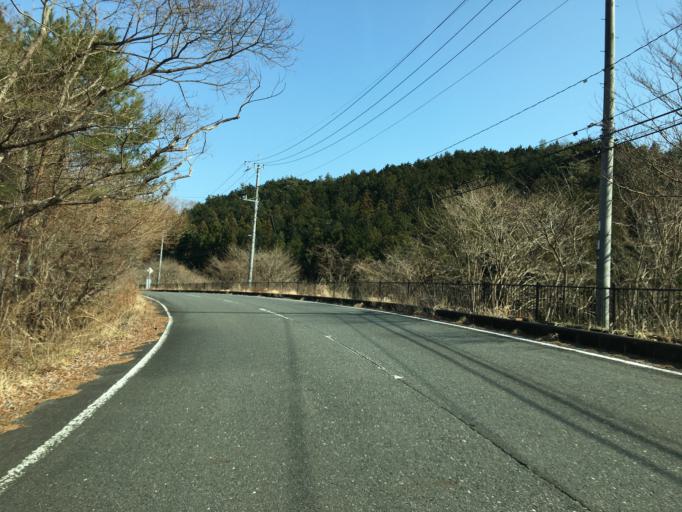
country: JP
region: Ibaraki
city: Kitaibaraki
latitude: 36.8060
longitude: 140.6299
